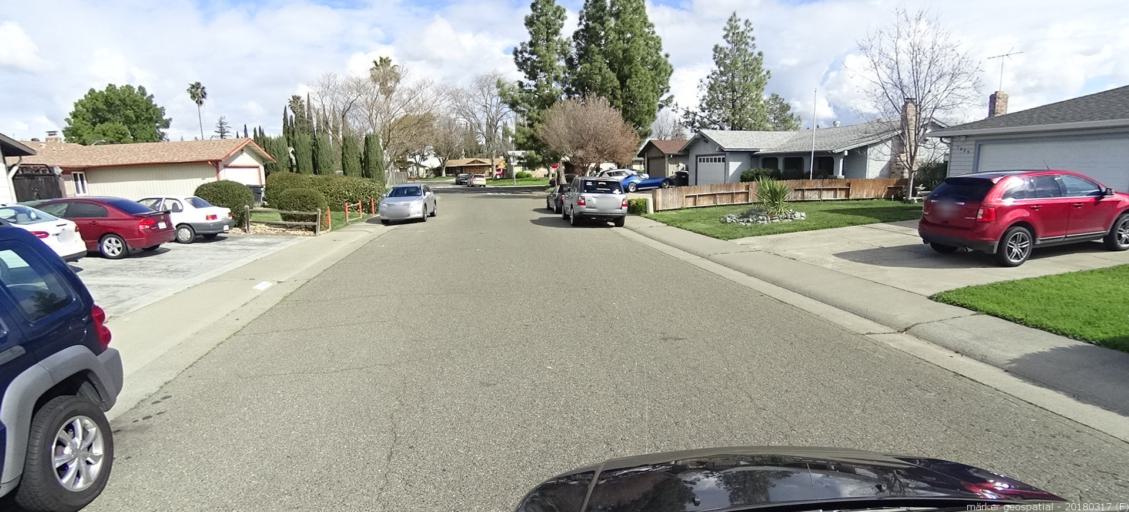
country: US
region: California
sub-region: Sacramento County
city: Florin
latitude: 38.4727
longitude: -121.3940
